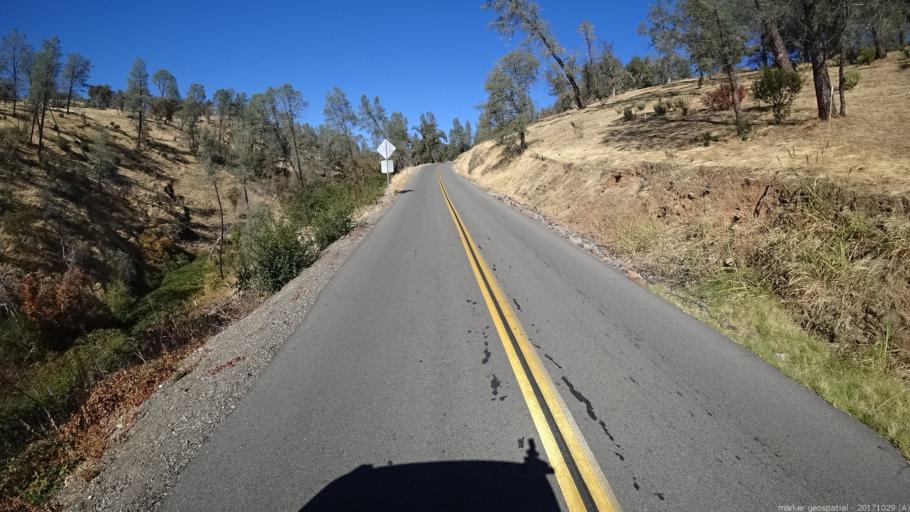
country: US
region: California
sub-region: Shasta County
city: Shasta
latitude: 40.4780
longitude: -122.6296
